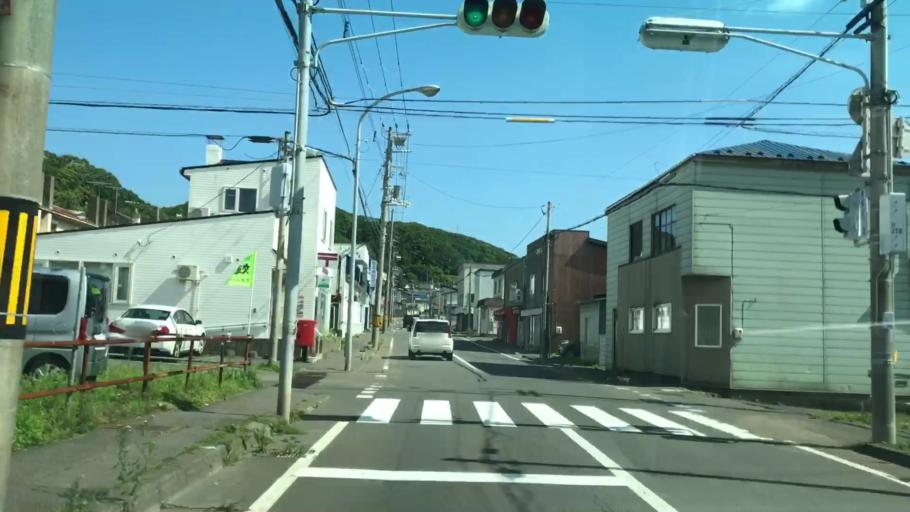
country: JP
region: Hokkaido
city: Muroran
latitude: 42.3112
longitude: 140.9948
